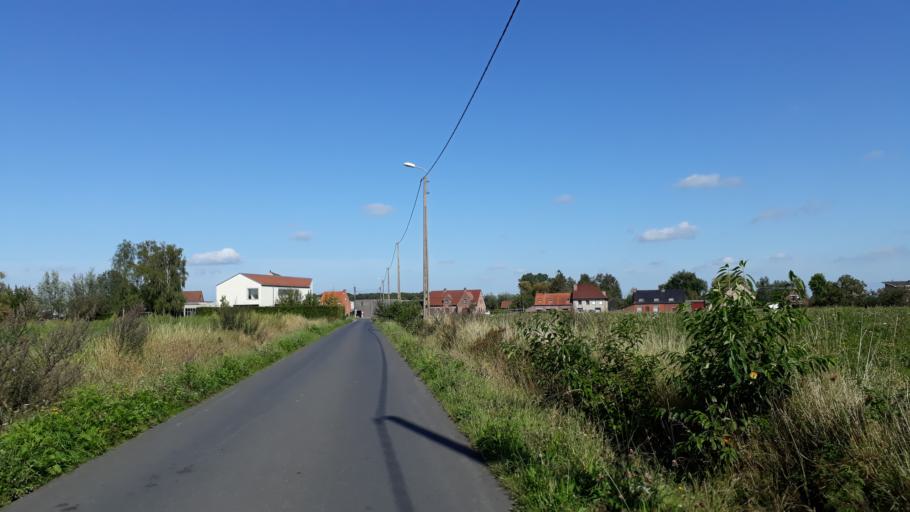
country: BE
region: Flanders
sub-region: Provincie West-Vlaanderen
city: Torhout
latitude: 51.0838
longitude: 3.1019
